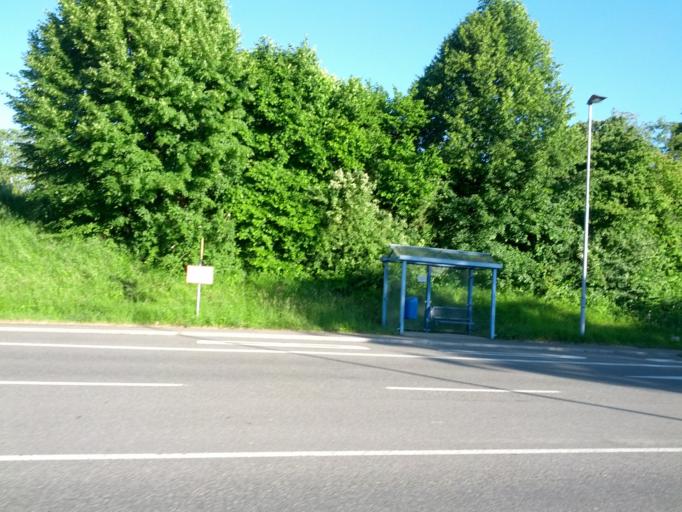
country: DE
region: Baden-Wuerttemberg
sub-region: Freiburg Region
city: Pfaffenweiler
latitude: 47.9440
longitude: 7.7364
